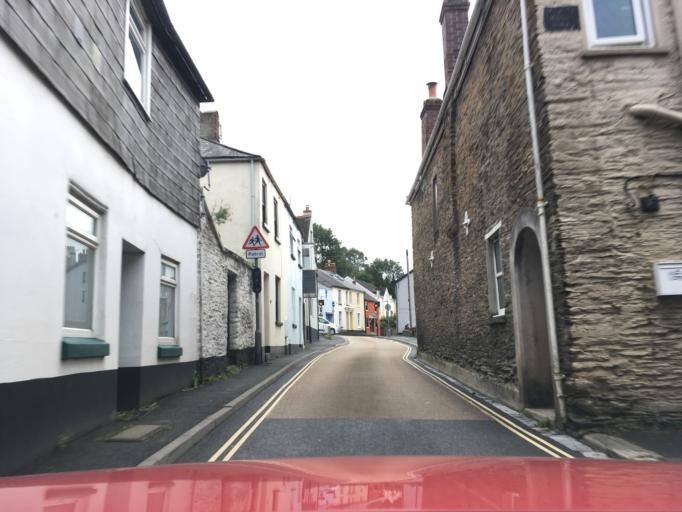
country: GB
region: England
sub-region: Devon
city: Kingsbridge
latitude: 50.2868
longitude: -3.7746
